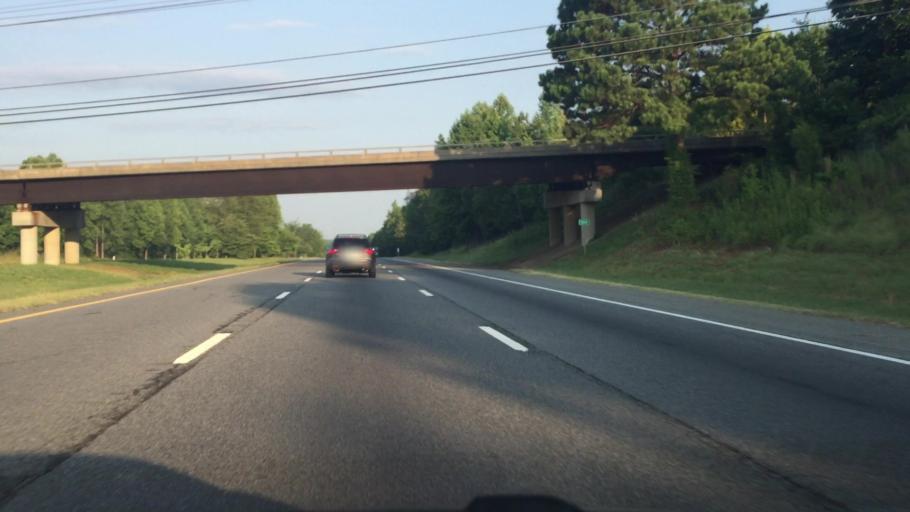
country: US
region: North Carolina
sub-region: Davidson County
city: Lexington
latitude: 35.7770
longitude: -80.2780
